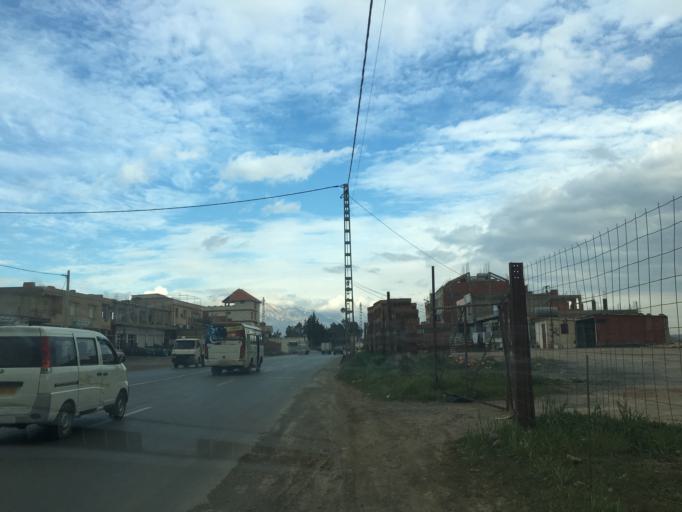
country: DZ
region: Bouira
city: Bouira
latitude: 36.3624
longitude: 3.8536
